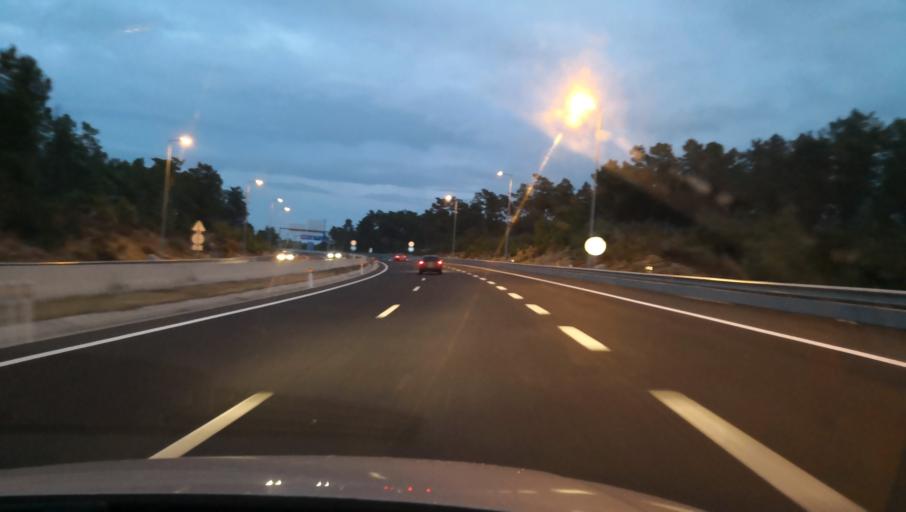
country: PT
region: Setubal
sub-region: Seixal
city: Amora
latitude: 38.6017
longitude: -9.1273
